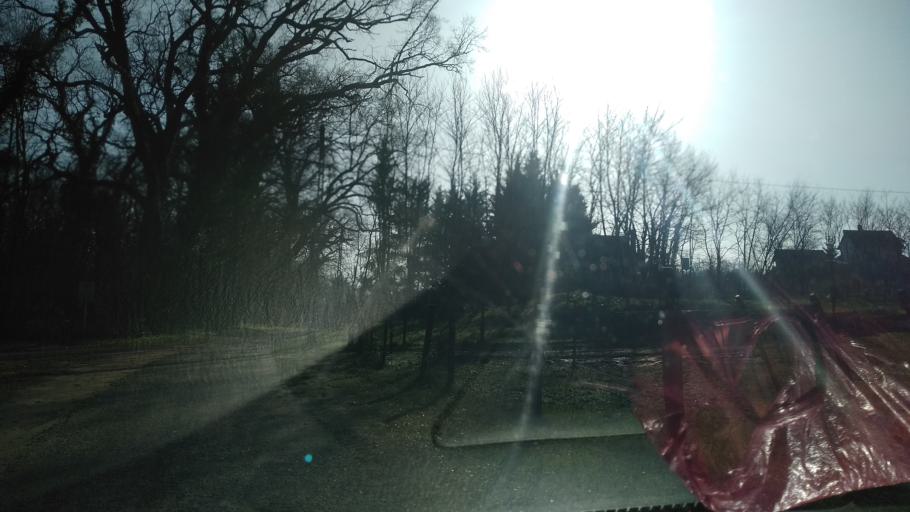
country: HU
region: Somogy
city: Barcs
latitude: 45.9542
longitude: 17.5084
